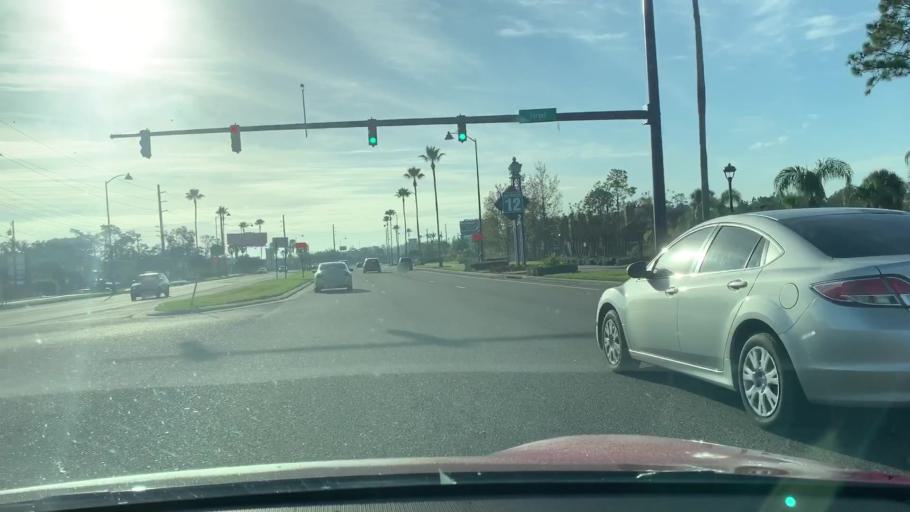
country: US
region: Florida
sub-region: Orange County
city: Hunters Creek
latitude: 28.3300
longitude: -81.4732
